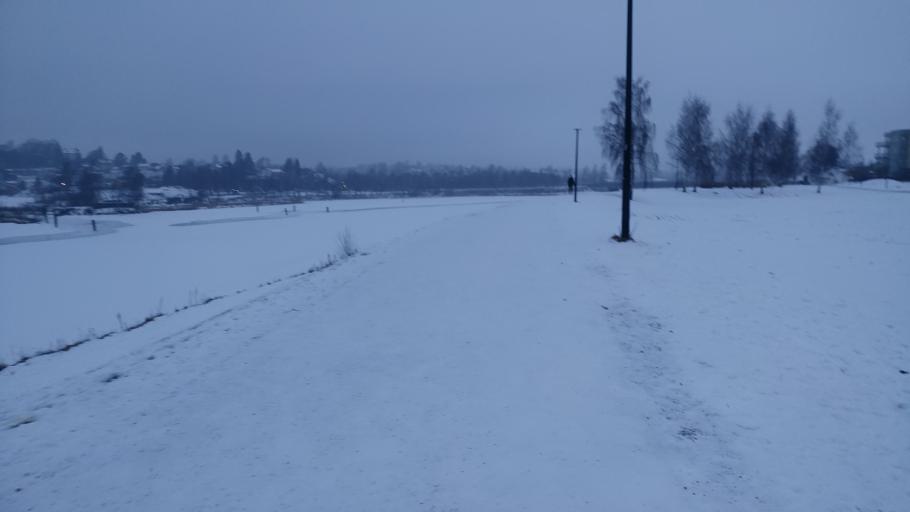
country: NO
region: Akershus
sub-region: Skedsmo
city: Lillestrom
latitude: 59.9546
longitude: 11.0331
